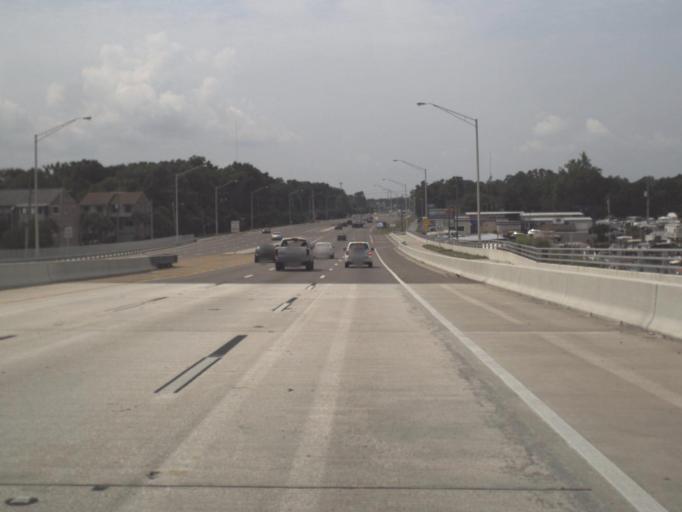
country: US
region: Florida
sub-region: Clay County
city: Orange Park
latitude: 30.1469
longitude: -81.7011
